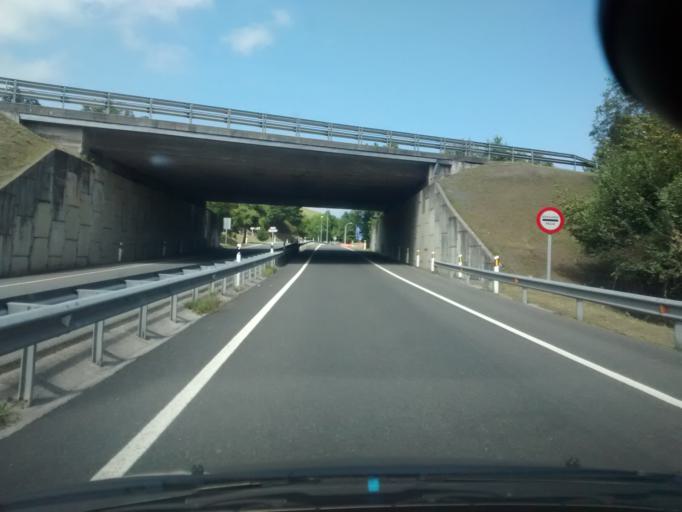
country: ES
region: Basque Country
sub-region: Provincia de Guipuzcoa
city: Cestona
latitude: 43.2648
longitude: -2.2723
